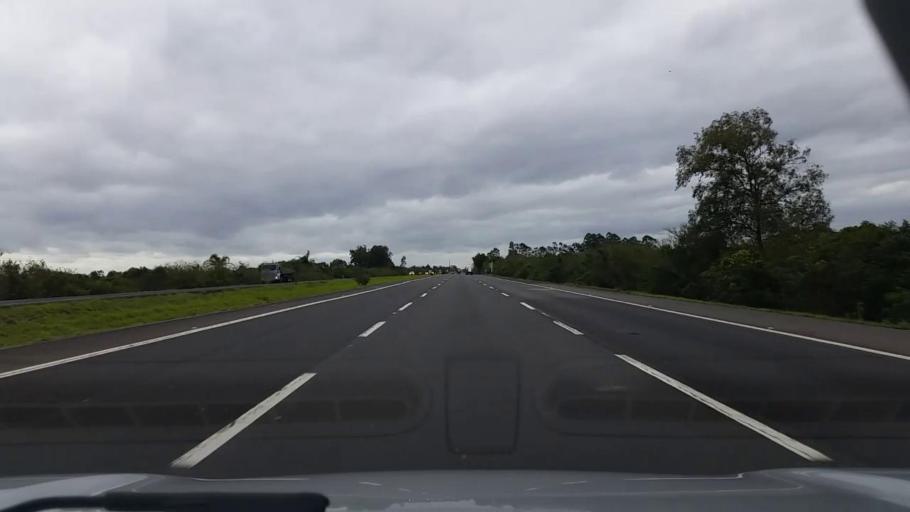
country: BR
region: Rio Grande do Sul
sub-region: Rolante
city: Rolante
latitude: -29.8836
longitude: -50.5522
